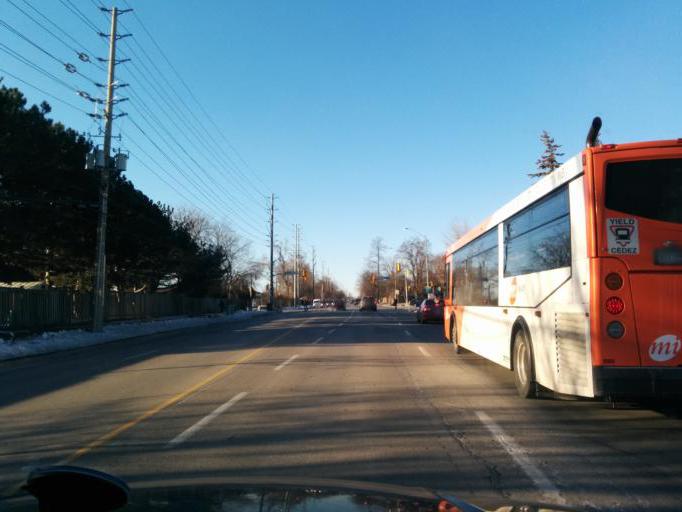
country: CA
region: Ontario
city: Mississauga
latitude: 43.5622
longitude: -79.6496
